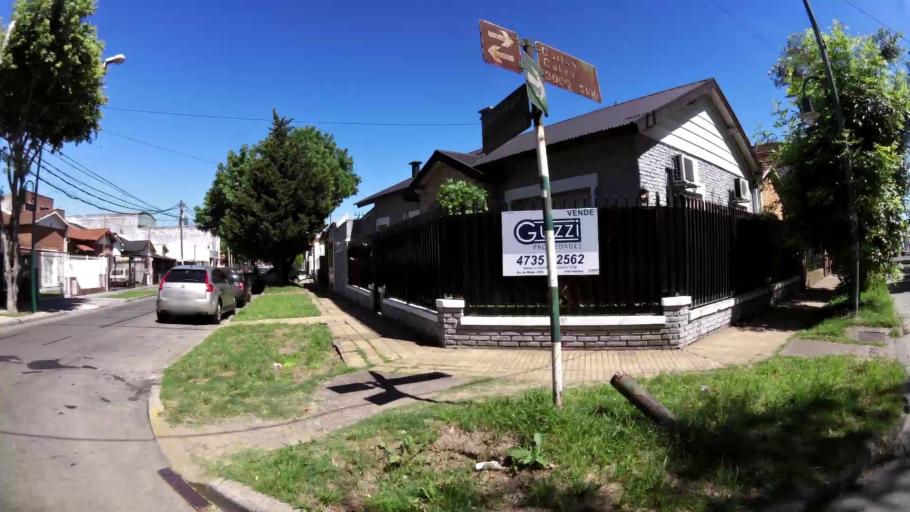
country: AR
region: Buenos Aires
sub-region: Partido de General San Martin
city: General San Martin
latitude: -34.5286
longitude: -58.5314
